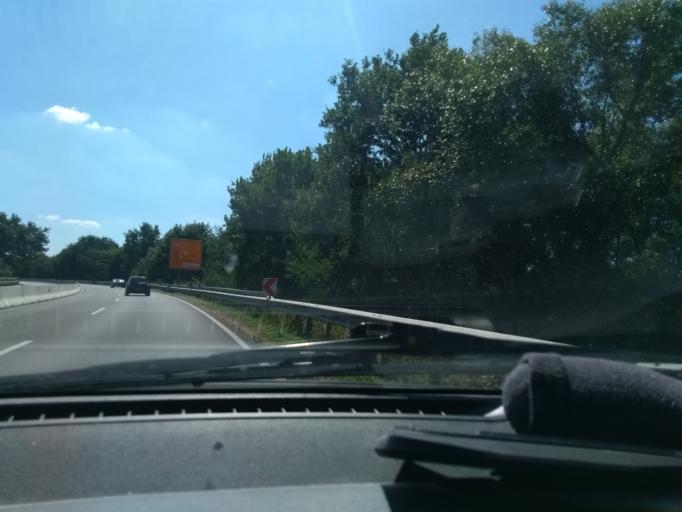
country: DE
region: Lower Saxony
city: Meppen
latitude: 52.6856
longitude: 7.2858
